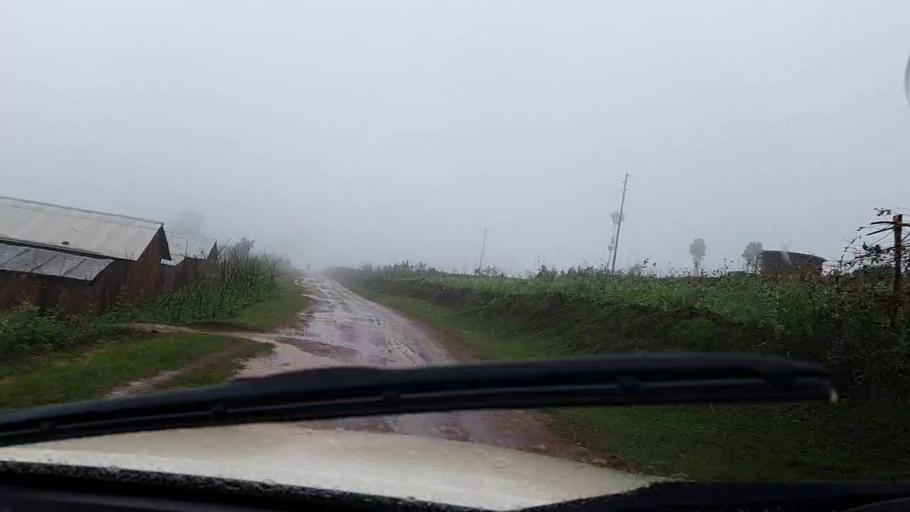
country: RW
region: Northern Province
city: Byumba
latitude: -1.7363
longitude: 30.0110
